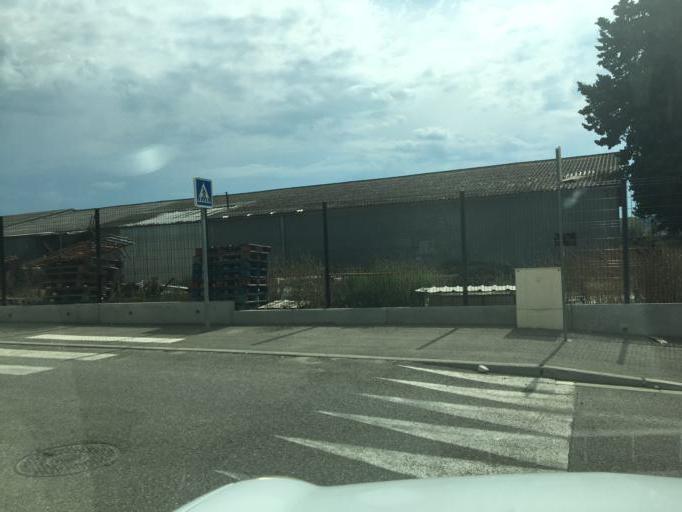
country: FR
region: Provence-Alpes-Cote d'Azur
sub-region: Departement des Bouches-du-Rhone
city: Bouc-Bel-Air
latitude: 43.4849
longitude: 5.3909
